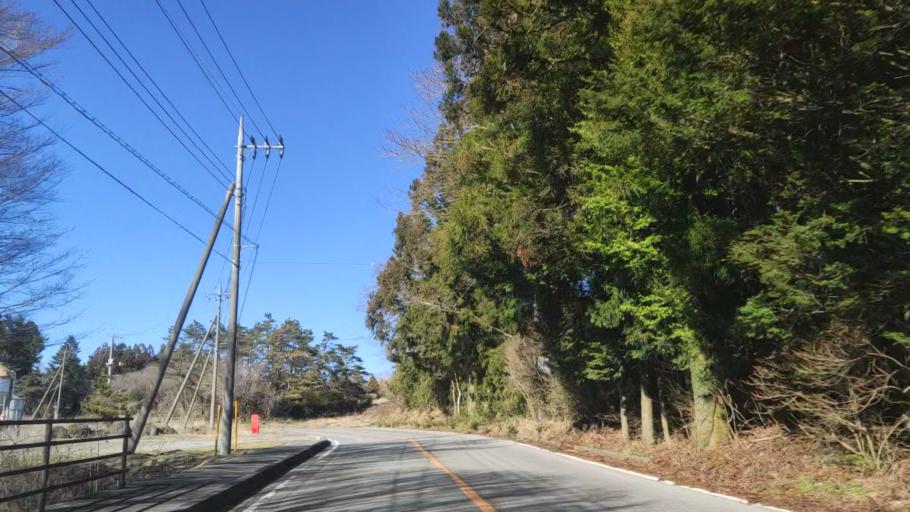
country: JP
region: Yamanashi
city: Fujikawaguchiko
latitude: 35.3988
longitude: 138.6117
